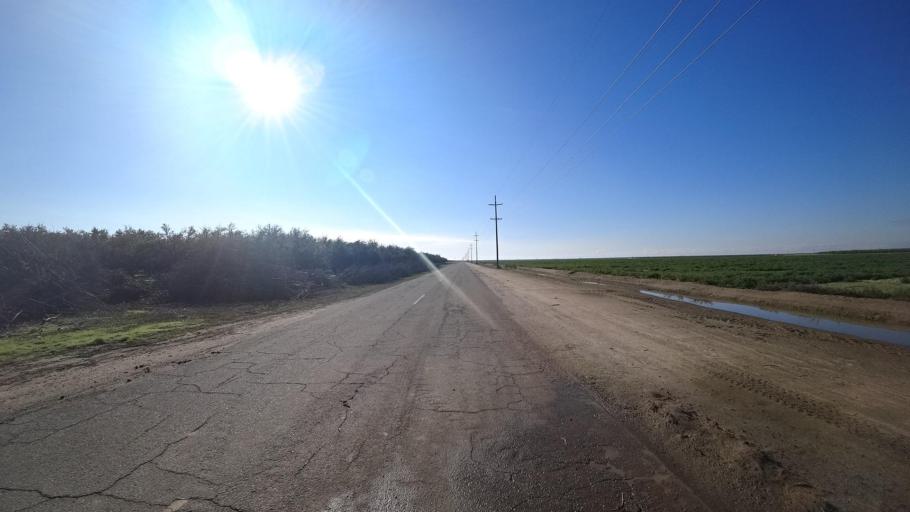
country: US
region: California
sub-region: Kern County
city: McFarland
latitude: 35.6815
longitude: -119.2765
